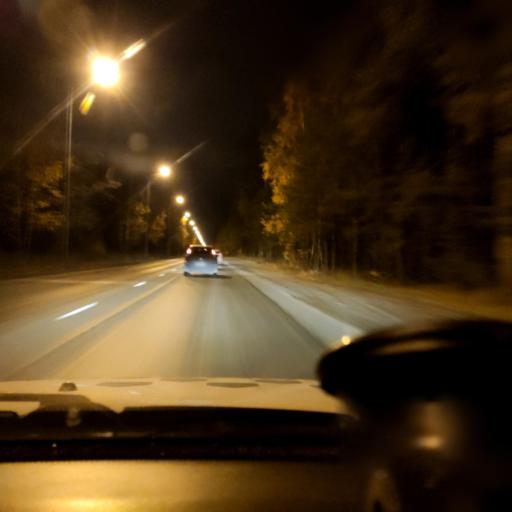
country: RU
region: Perm
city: Perm
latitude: 58.0590
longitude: 56.2542
